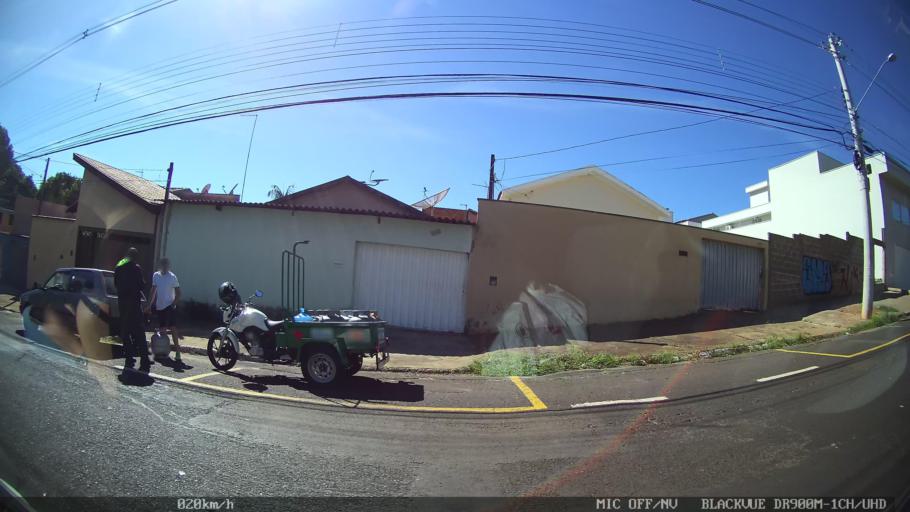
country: BR
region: Sao Paulo
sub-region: Franca
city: Franca
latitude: -20.5508
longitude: -47.3723
